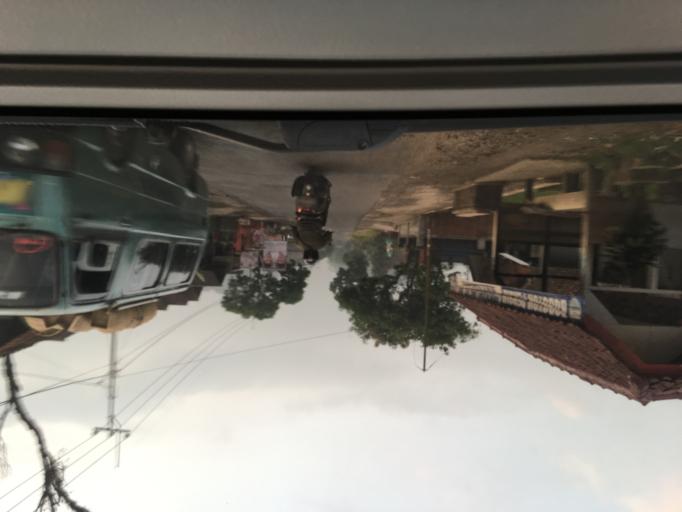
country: ID
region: West Java
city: Pasireurih
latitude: -7.1838
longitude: 108.1970
